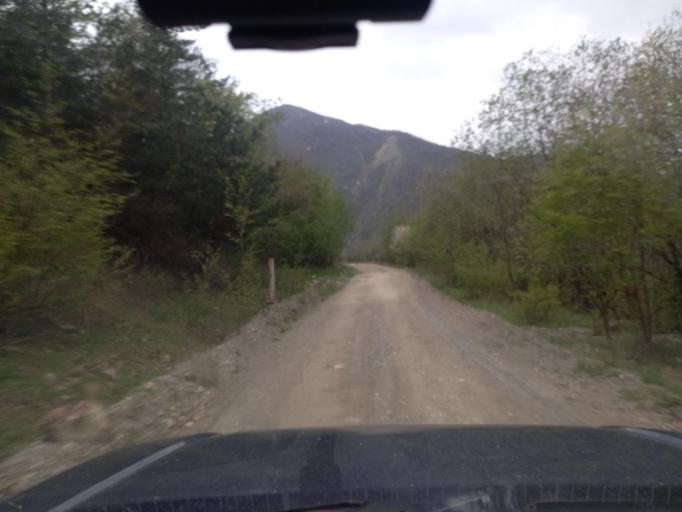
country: RU
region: North Ossetia
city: Mizur
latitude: 42.8528
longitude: 44.1646
